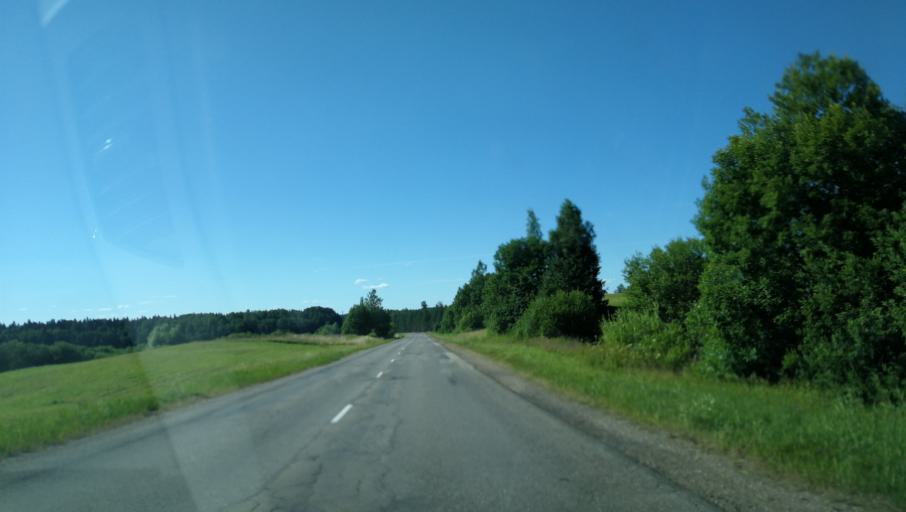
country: LV
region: Jaunpiebalga
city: Jaunpiebalga
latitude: 56.9890
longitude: 26.0146
